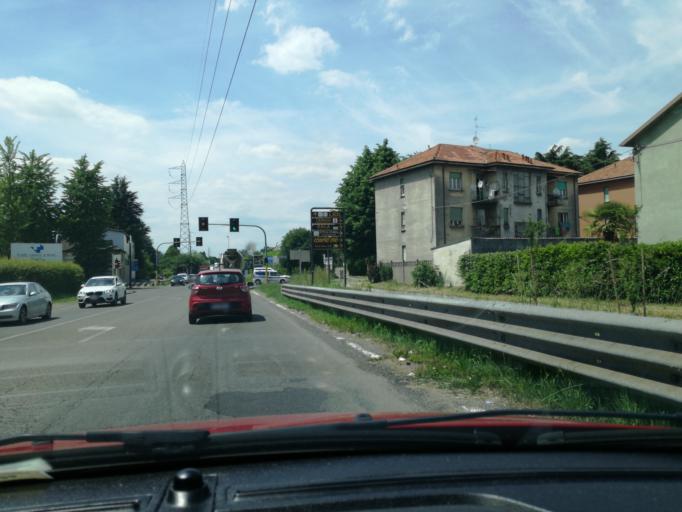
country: IT
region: Lombardy
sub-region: Provincia di Monza e Brianza
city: Bovisio-Masciago
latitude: 45.6168
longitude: 9.1477
